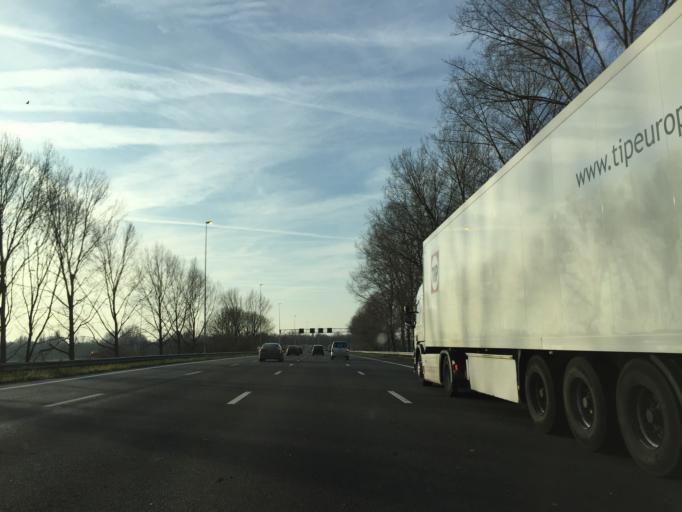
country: NL
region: South Holland
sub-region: Bodegraven-Reeuwijk
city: Reeuwijk
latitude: 52.0452
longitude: 4.7113
